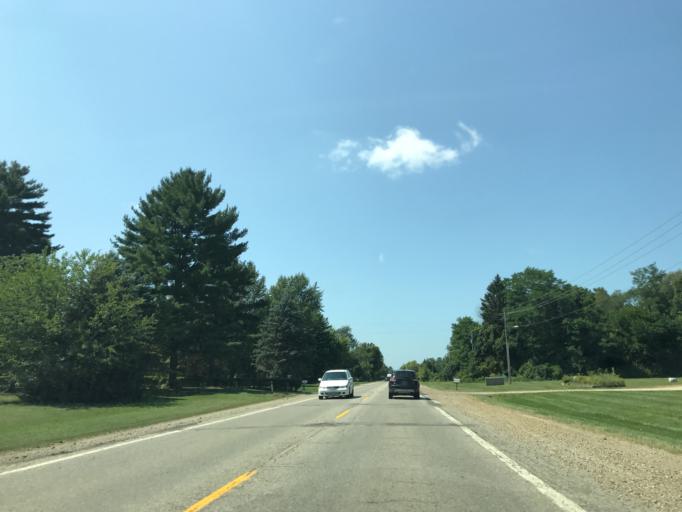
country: US
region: Michigan
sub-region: Berrien County
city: Buchanan
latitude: 41.8051
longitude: -86.3328
